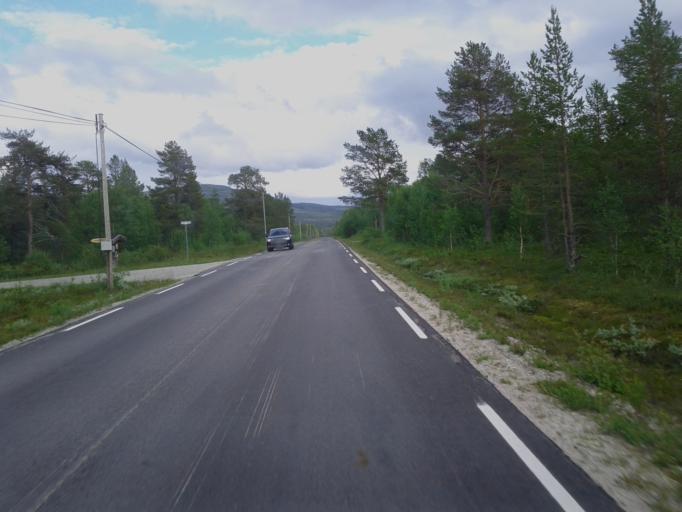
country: NO
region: Sor-Trondelag
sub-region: Roros
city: Roros
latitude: 62.3055
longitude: 11.7029
